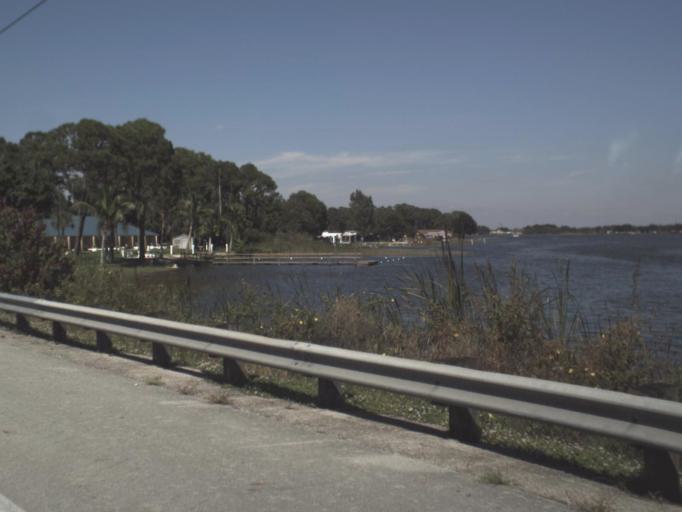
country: US
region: Florida
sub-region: Highlands County
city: Lake Placid
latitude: 27.2521
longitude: -81.3400
